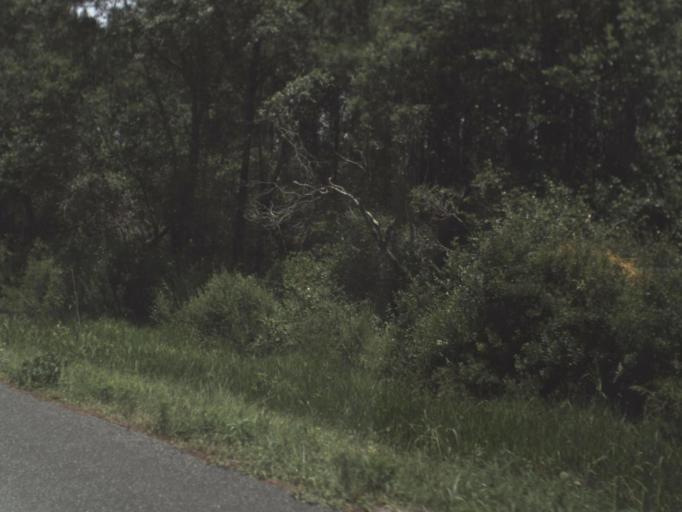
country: US
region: Florida
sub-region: Lafayette County
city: Mayo
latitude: 30.0081
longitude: -83.1926
